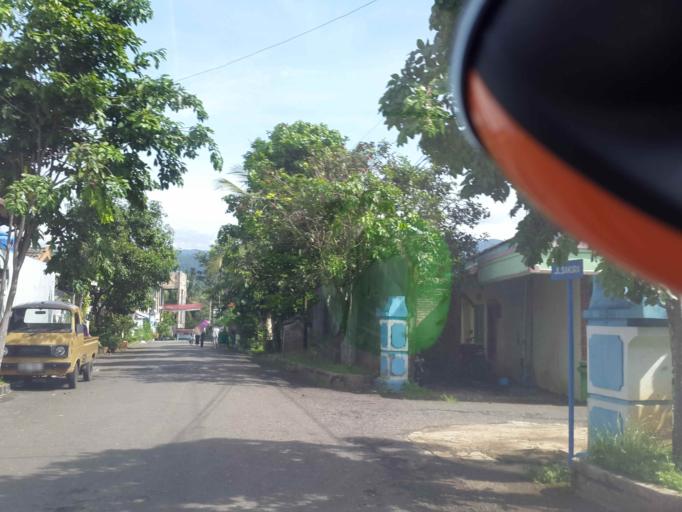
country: ID
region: Central Java
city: Wonosobo
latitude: -7.3904
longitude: 109.7254
